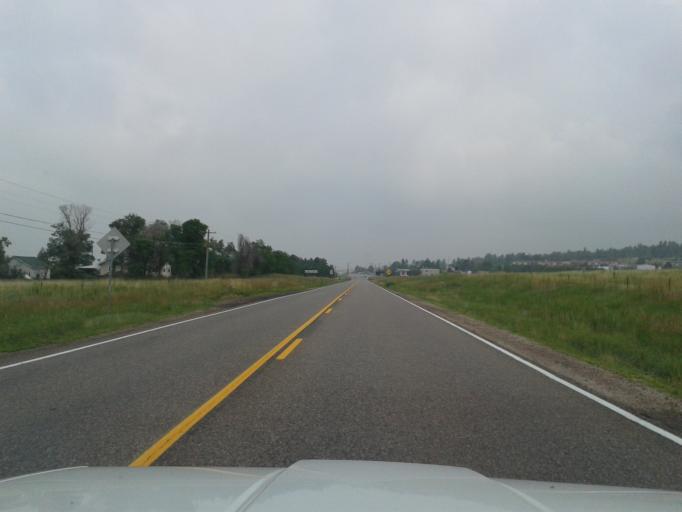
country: US
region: Colorado
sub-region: Douglas County
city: The Pinery
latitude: 39.3851
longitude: -104.7517
